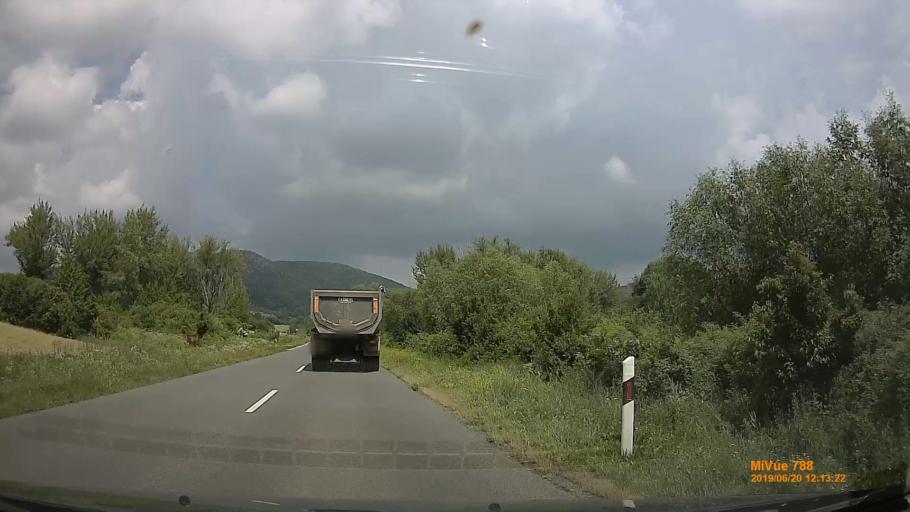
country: HU
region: Baranya
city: Hosszuheteny
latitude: 46.1574
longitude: 18.3431
